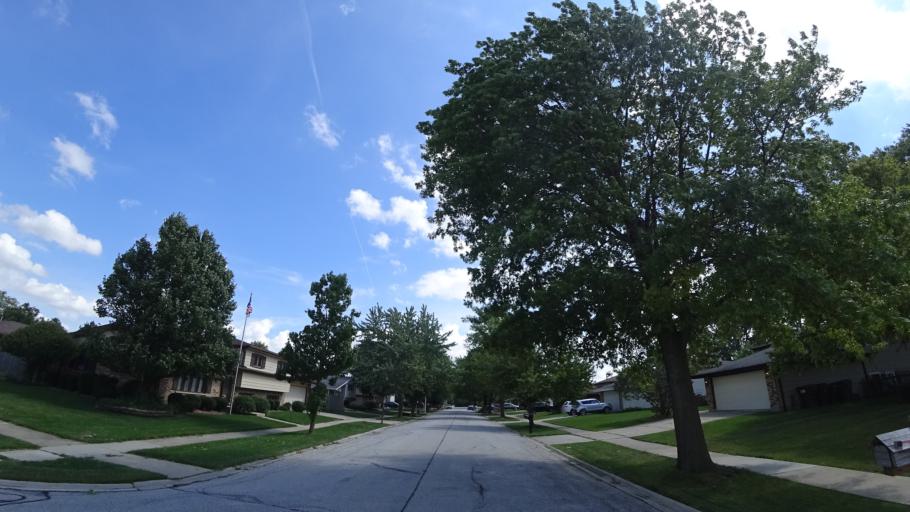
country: US
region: Illinois
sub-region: Cook County
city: Tinley Park
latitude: 41.5624
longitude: -87.7763
